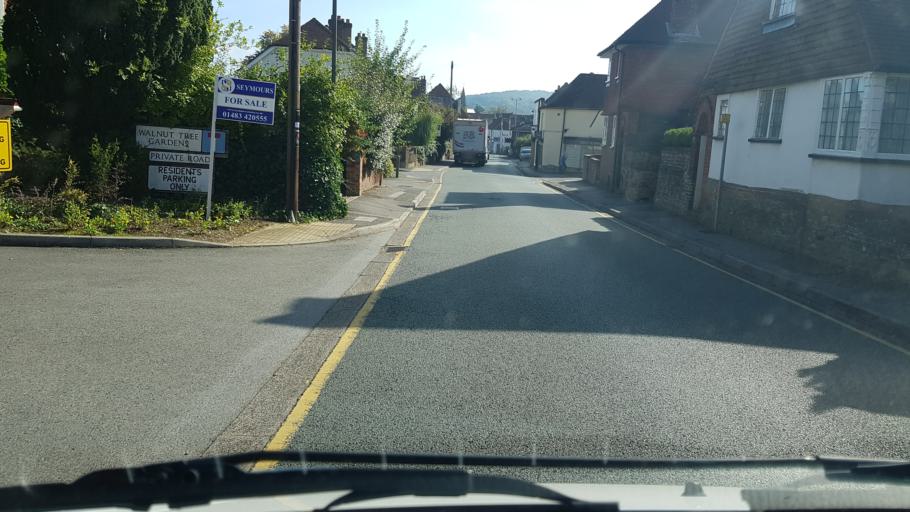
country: GB
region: England
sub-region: Surrey
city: Godalming
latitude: 51.1964
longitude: -0.6077
